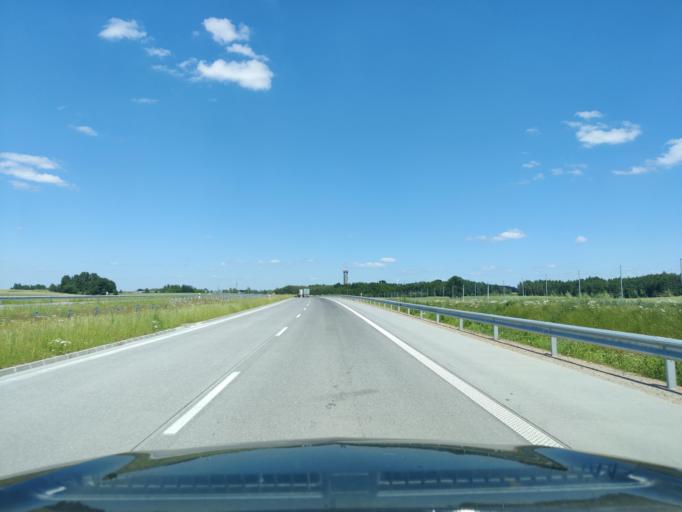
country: PL
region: Masovian Voivodeship
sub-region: Powiat mlawski
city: Mlawa
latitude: 53.0857
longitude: 20.4019
